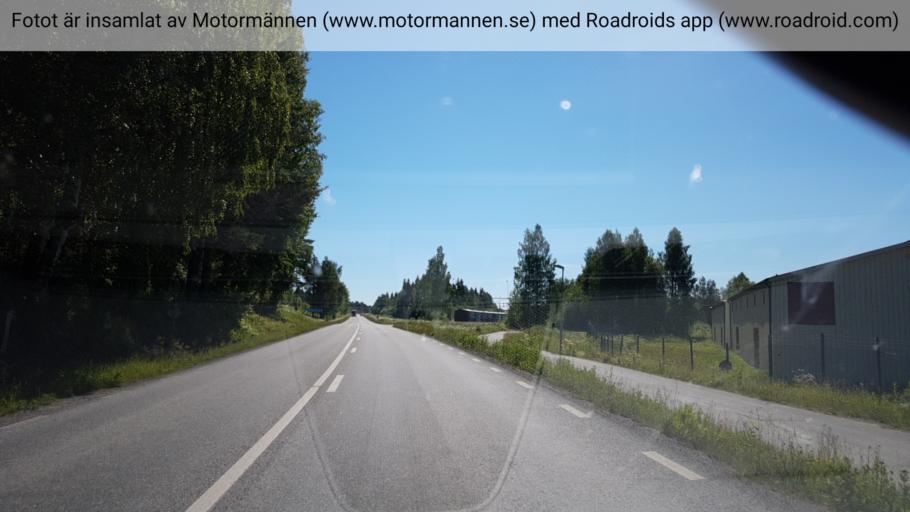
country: SE
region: Norrbotten
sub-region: Bodens Kommun
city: Boden
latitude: 65.8308
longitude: 21.6258
